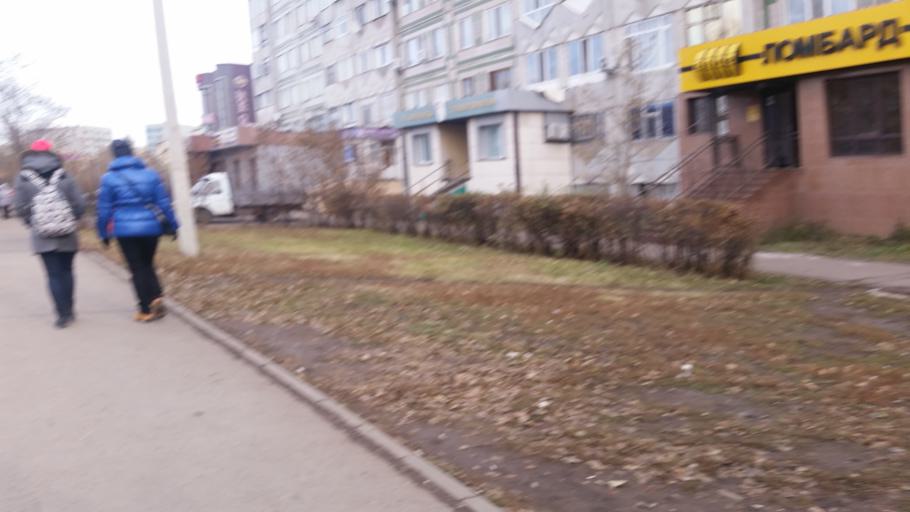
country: KZ
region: Astana Qalasy
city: Astana
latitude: 51.1515
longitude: 71.4744
